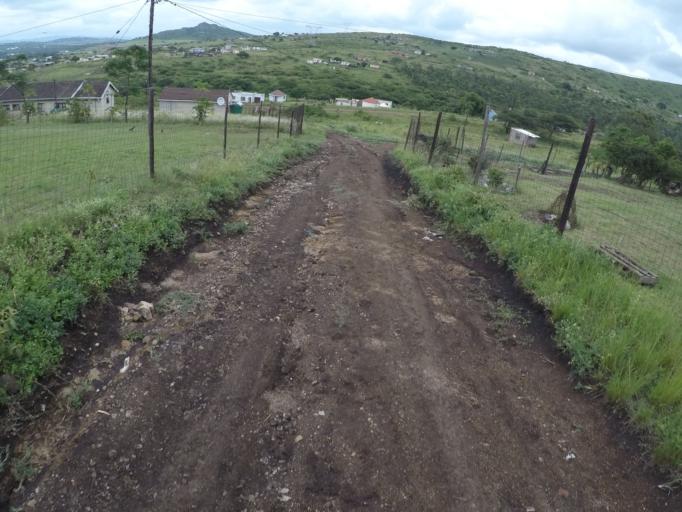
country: ZA
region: KwaZulu-Natal
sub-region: uThungulu District Municipality
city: Empangeni
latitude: -28.7074
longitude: 31.8498
